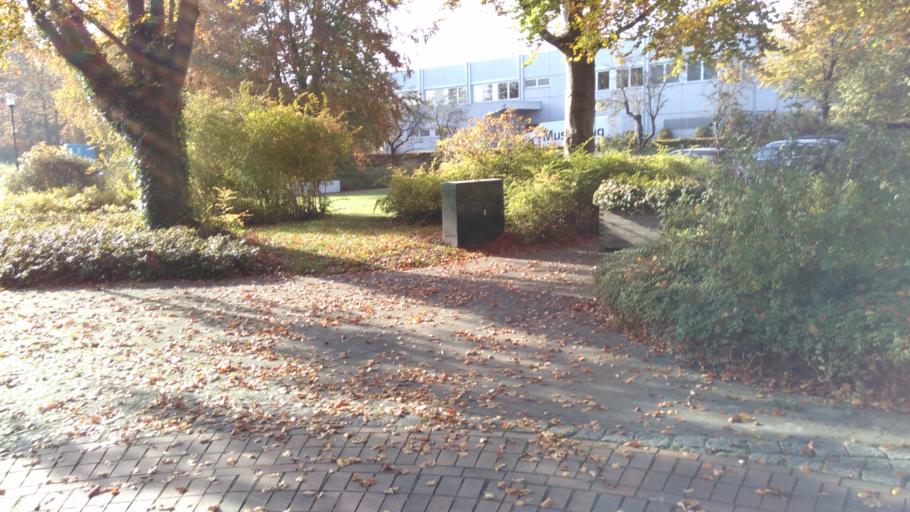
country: DE
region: North Rhine-Westphalia
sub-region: Regierungsbezirk Detmold
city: Rheda-Wiedenbruck
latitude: 51.8440
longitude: 8.2990
